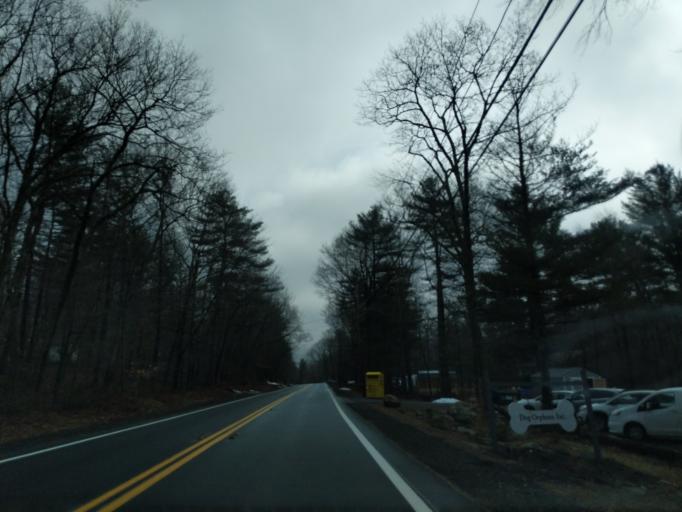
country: US
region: Massachusetts
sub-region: Worcester County
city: Douglas
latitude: 42.0543
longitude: -71.7560
